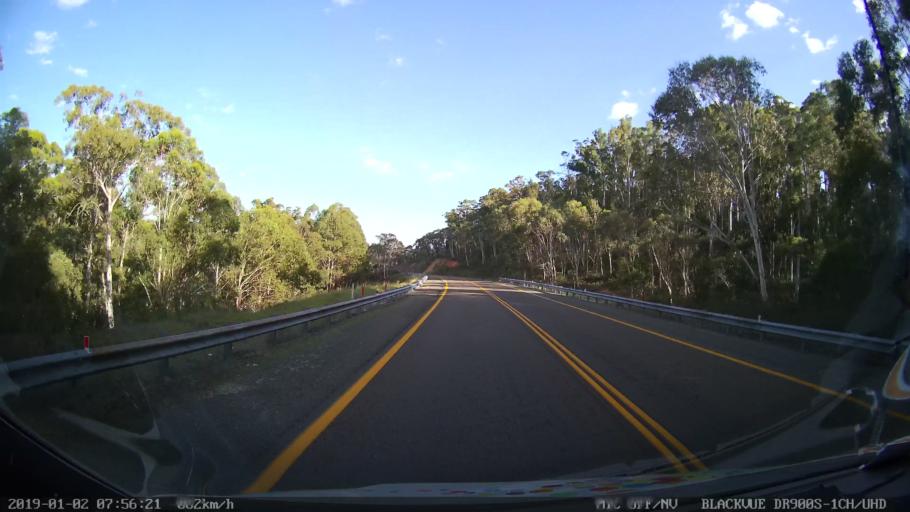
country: AU
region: New South Wales
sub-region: Tumut Shire
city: Tumut
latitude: -35.6718
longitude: 148.4857
